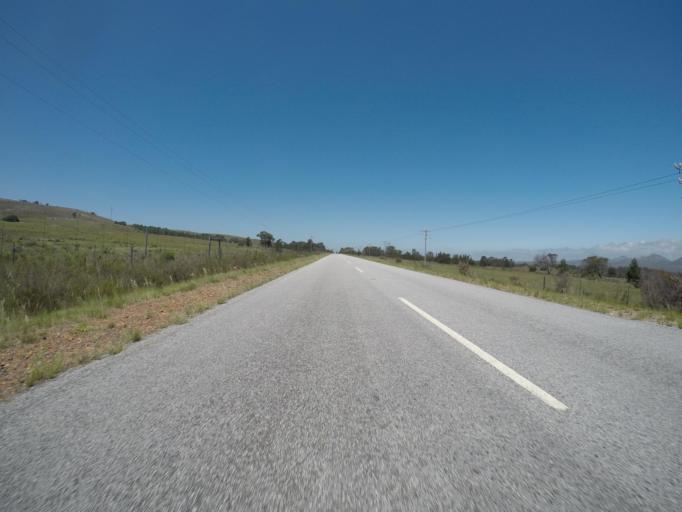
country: ZA
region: Eastern Cape
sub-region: Cacadu District Municipality
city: Kareedouw
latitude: -33.9674
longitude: 24.4503
